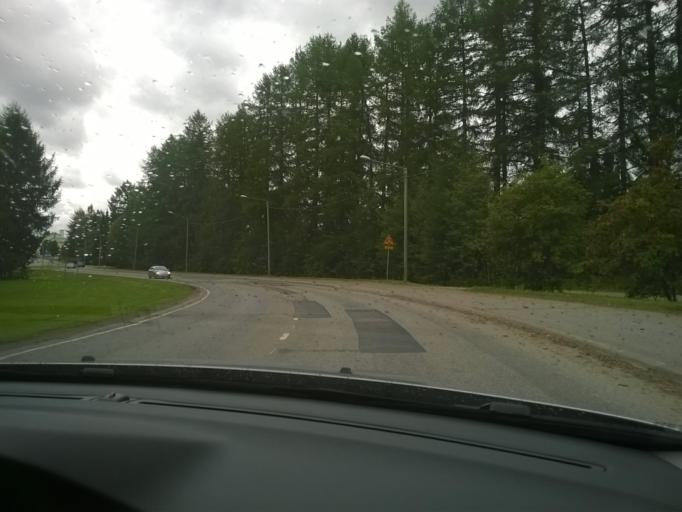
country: FI
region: Kainuu
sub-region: Kehys-Kainuu
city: Kuhmo
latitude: 64.1269
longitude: 29.5020
